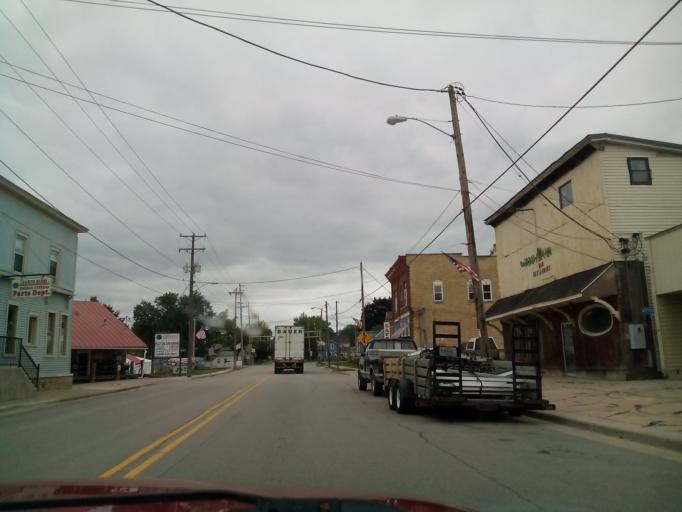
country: US
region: Wisconsin
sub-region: Outagamie County
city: Hortonville
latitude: 44.2731
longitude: -88.6786
